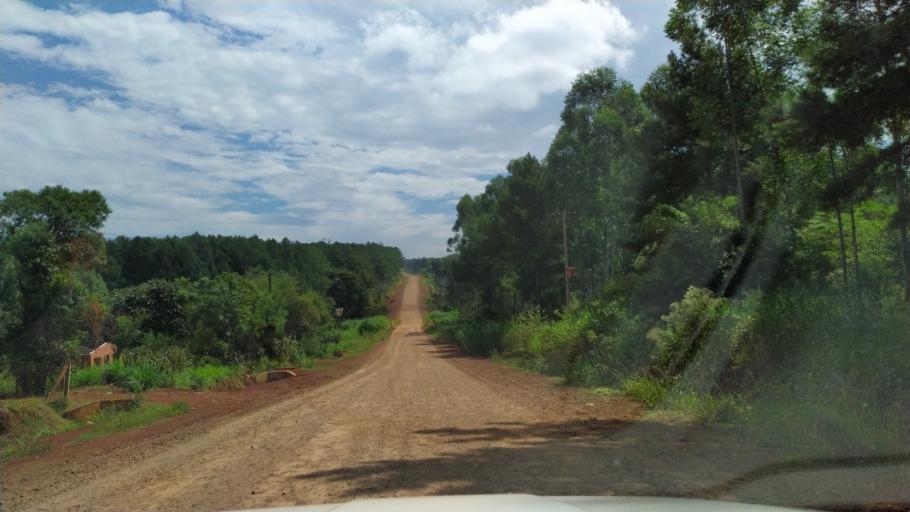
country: AR
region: Misiones
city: Puerto Piray
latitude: -26.5355
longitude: -54.6540
